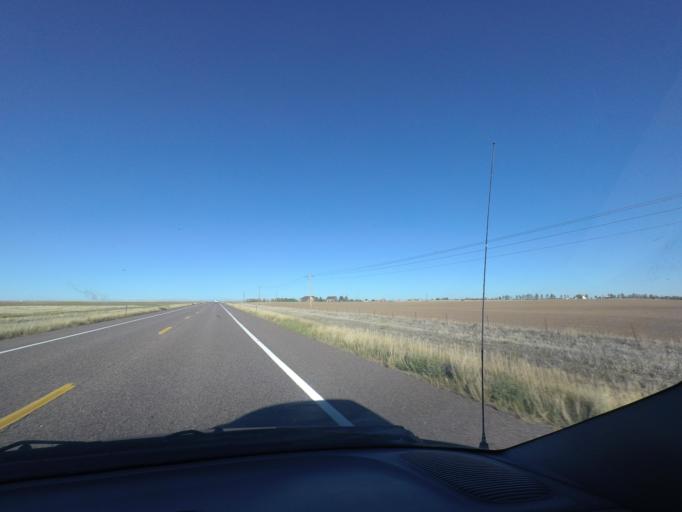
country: US
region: Colorado
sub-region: Arapahoe County
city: Byers
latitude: 39.7396
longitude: -104.1496
